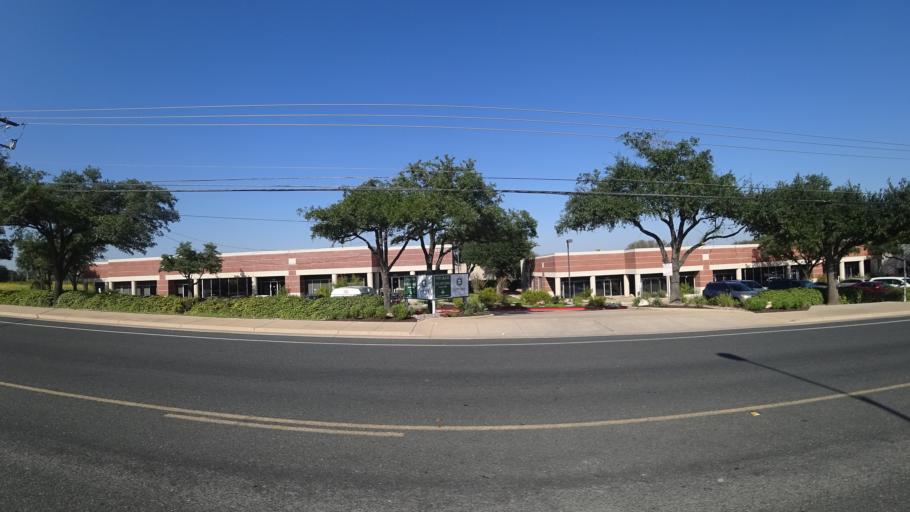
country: US
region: Texas
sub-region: Travis County
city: Austin
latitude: 30.3380
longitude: -97.6847
